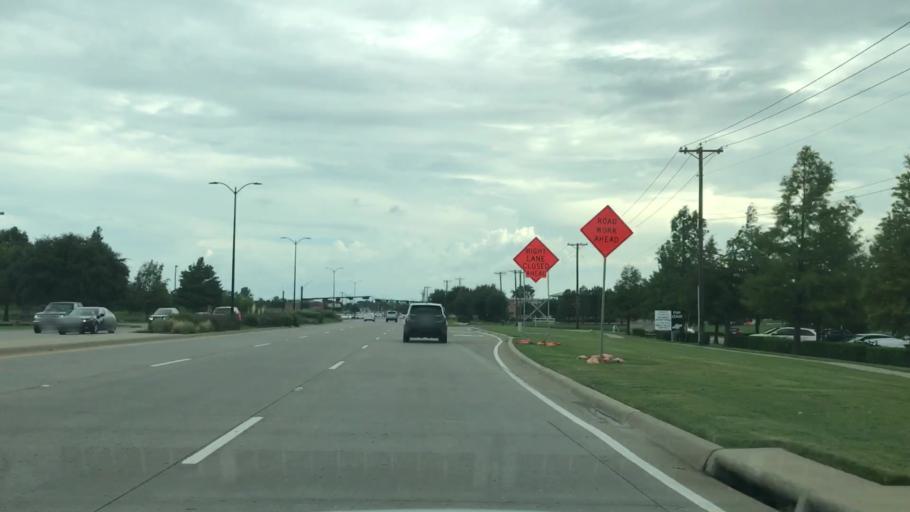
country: US
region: Texas
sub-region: Collin County
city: Frisco
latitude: 33.1307
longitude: -96.8048
